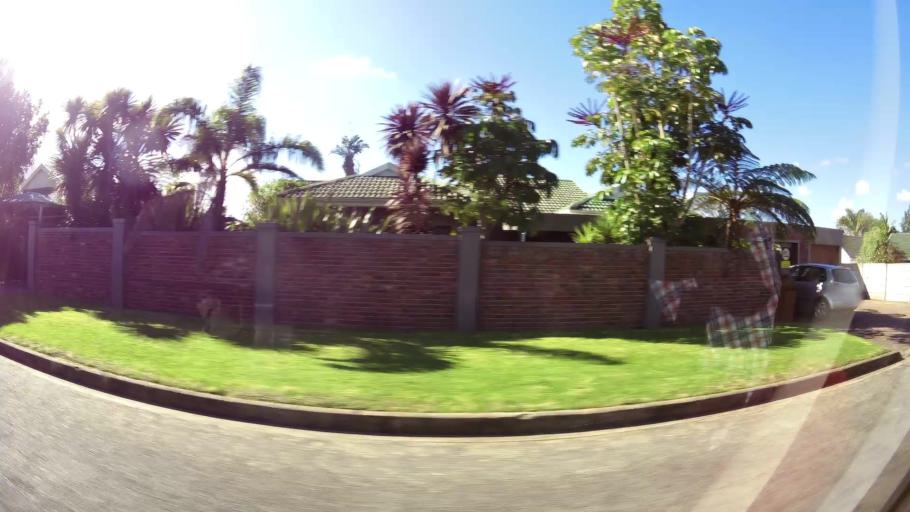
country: ZA
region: Western Cape
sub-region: Eden District Municipality
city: George
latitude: -33.9528
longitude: 22.4322
